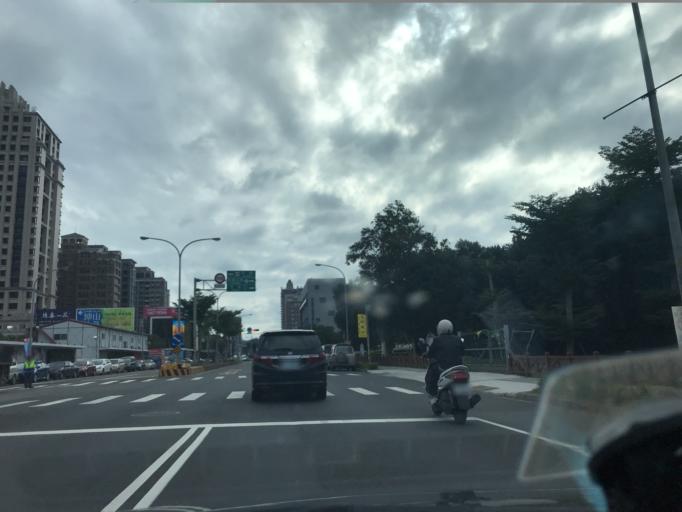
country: TW
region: Taiwan
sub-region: Hsinchu
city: Zhubei
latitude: 24.8230
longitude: 121.0232
